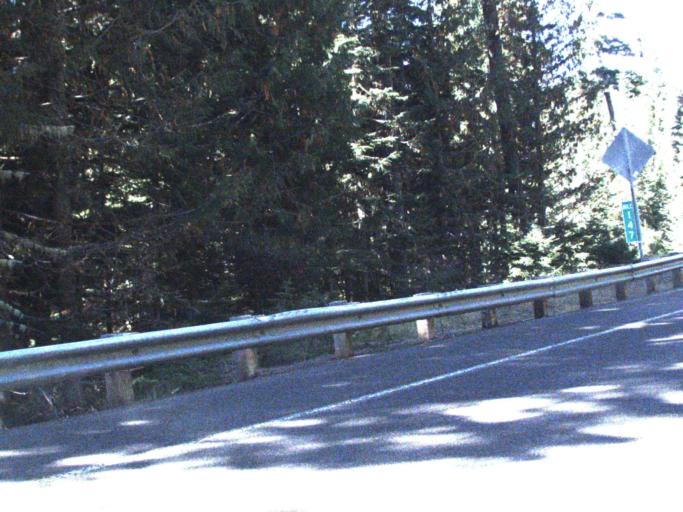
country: US
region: Washington
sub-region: Yakima County
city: Tieton
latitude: 46.6390
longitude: -121.4542
